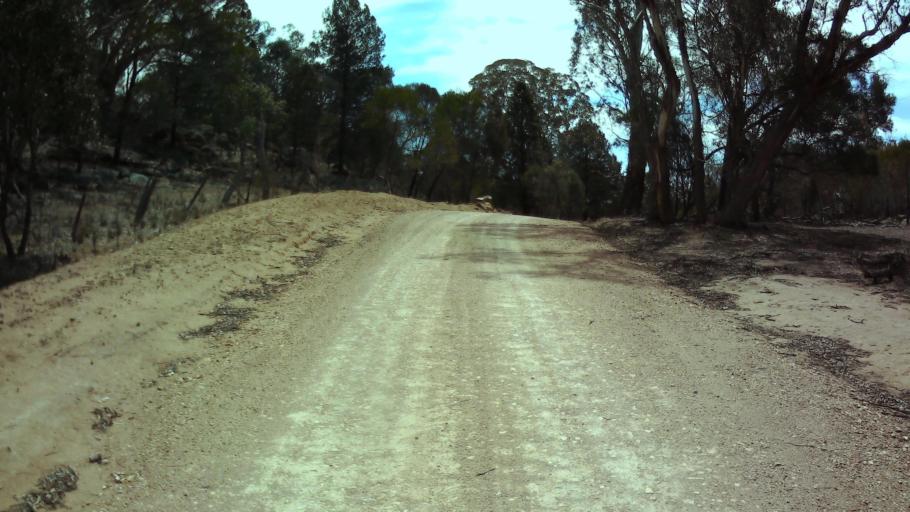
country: AU
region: New South Wales
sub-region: Weddin
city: Grenfell
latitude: -33.7450
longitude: 148.1818
